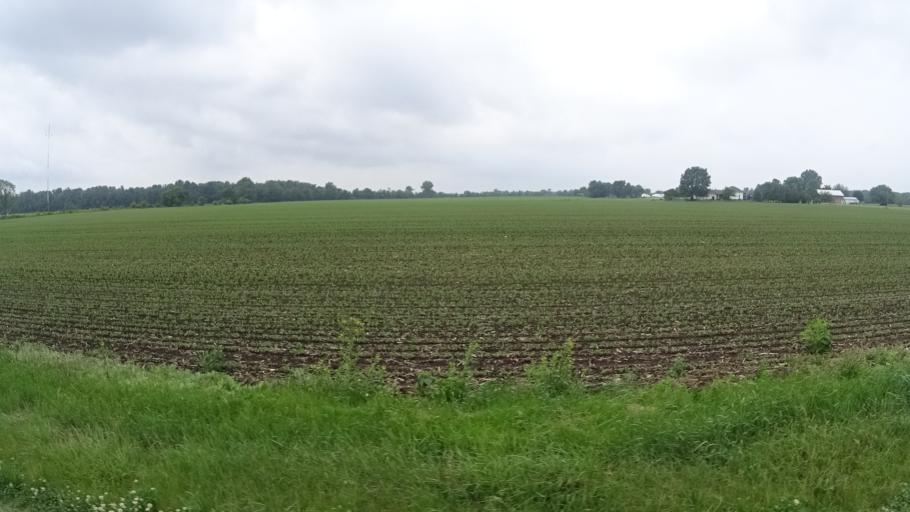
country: US
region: Ohio
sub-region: Huron County
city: Bellevue
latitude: 41.3605
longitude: -82.7948
